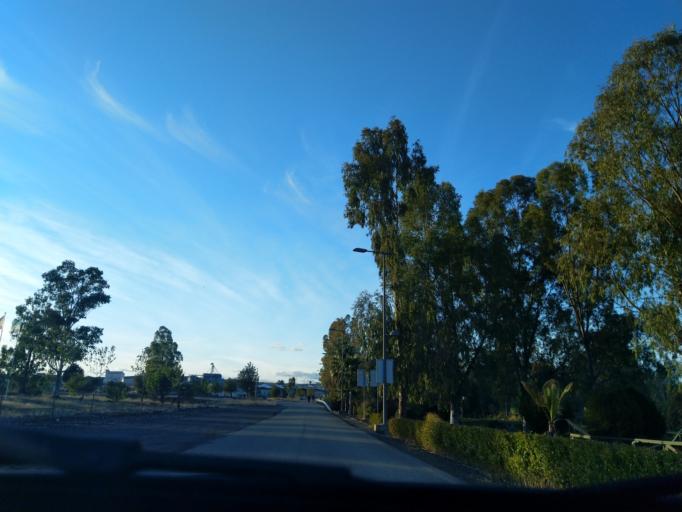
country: ES
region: Extremadura
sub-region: Provincia de Badajoz
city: Berlanga
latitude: 38.2750
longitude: -5.8189
